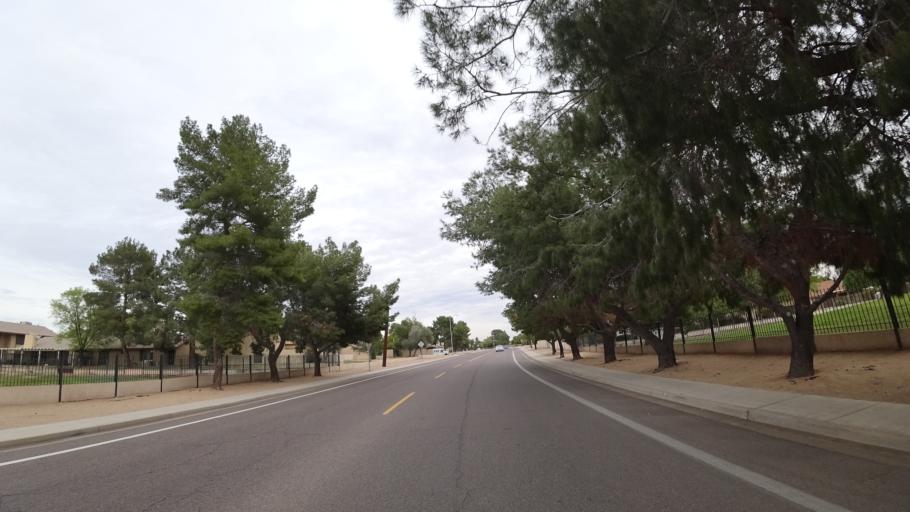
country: US
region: Arizona
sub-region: Maricopa County
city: Peoria
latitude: 33.6472
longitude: -112.1585
